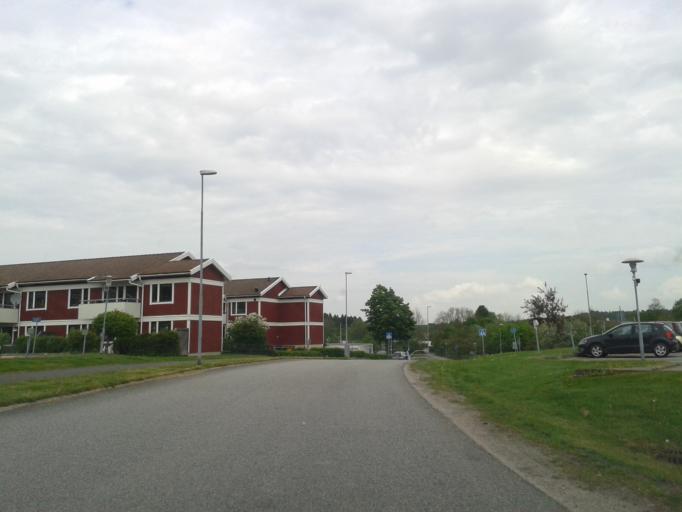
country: SE
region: Vaestra Goetaland
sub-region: Kungalvs Kommun
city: Kungalv
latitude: 57.8845
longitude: 11.9598
